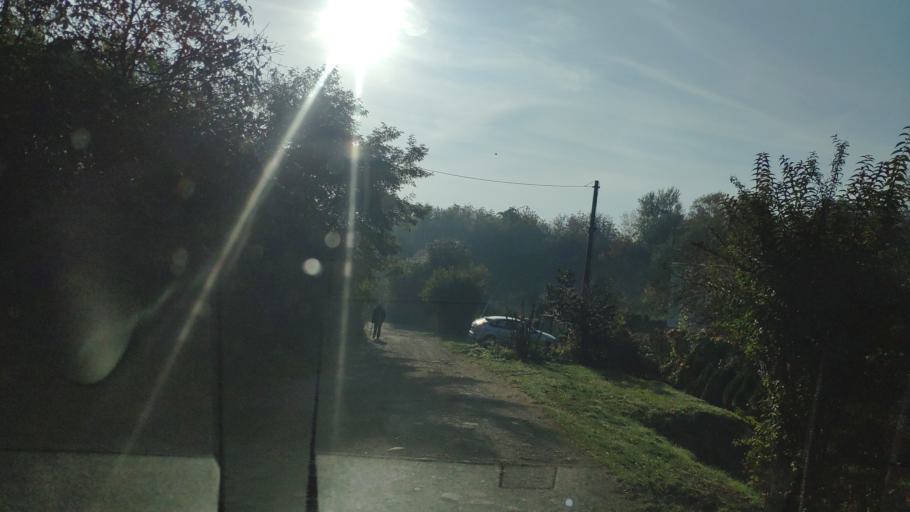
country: SK
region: Kosicky
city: Kosice
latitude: 48.7255
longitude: 21.2261
